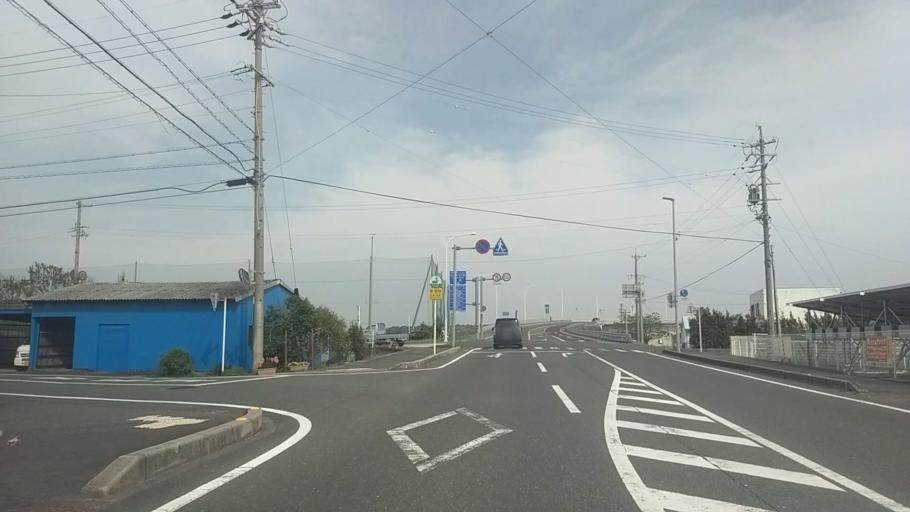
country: JP
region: Shizuoka
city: Kosai-shi
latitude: 34.7337
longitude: 137.6202
